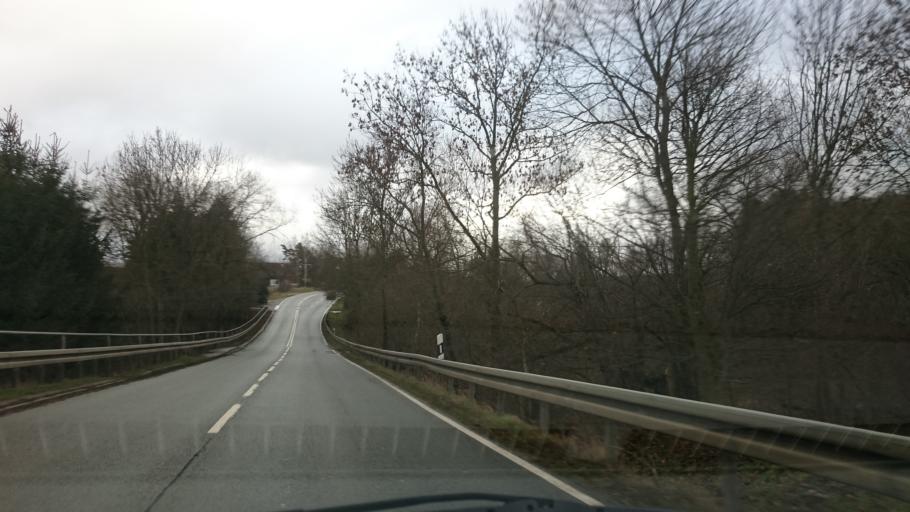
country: DE
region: Saxony
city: Kirchberg
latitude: 50.6465
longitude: 12.5637
